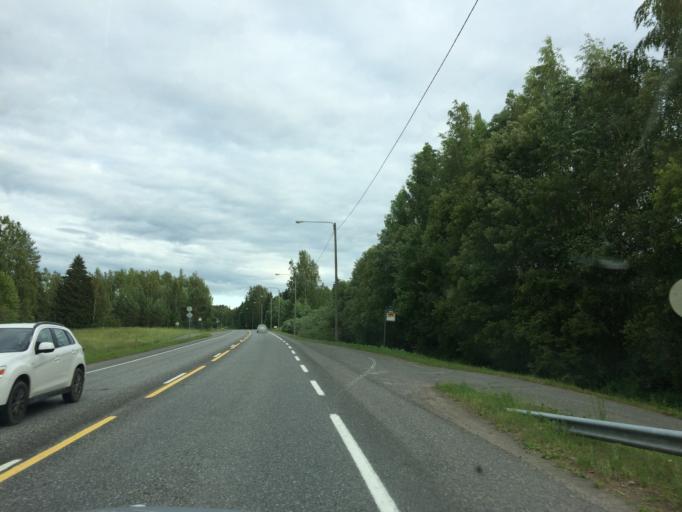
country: FI
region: Haeme
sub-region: Haemeenlinna
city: Haemeenlinna
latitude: 60.9616
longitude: 24.4829
